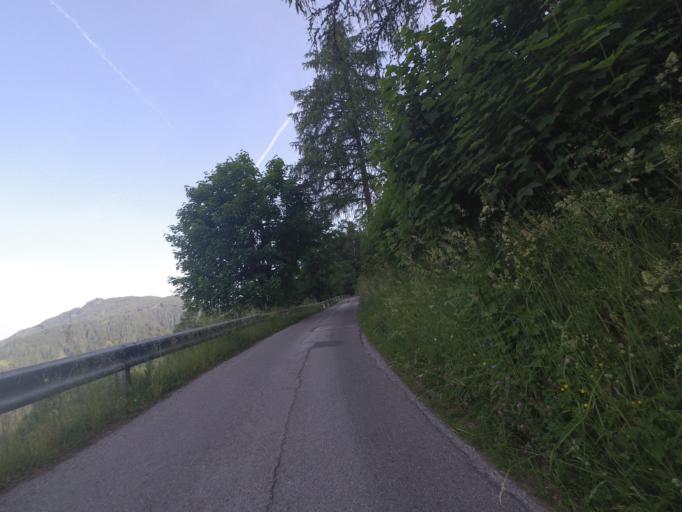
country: AT
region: Salzburg
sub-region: Politischer Bezirk Sankt Johann im Pongau
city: Muhlbach am Hochkonig
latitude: 47.3437
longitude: 13.1271
